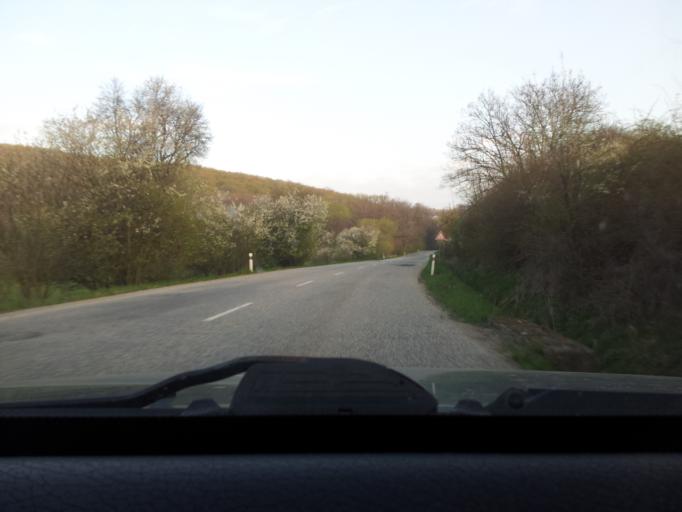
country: SK
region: Nitriansky
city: Tlmace
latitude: 48.2771
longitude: 18.5020
